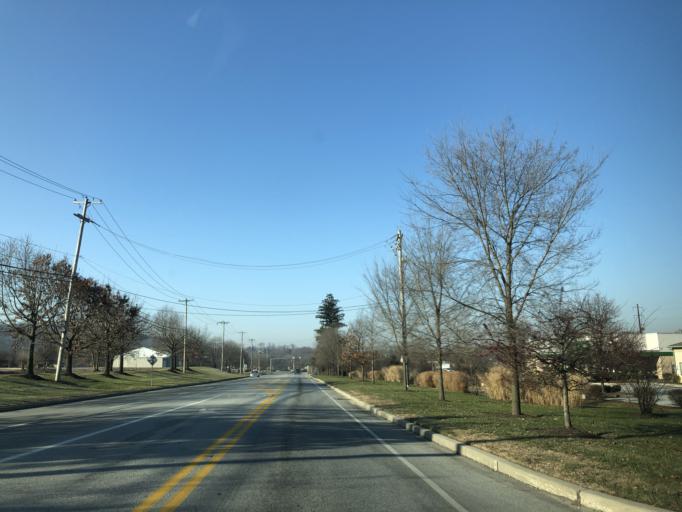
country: US
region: Pennsylvania
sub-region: Chester County
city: Downingtown
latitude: 40.0013
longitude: -75.6979
